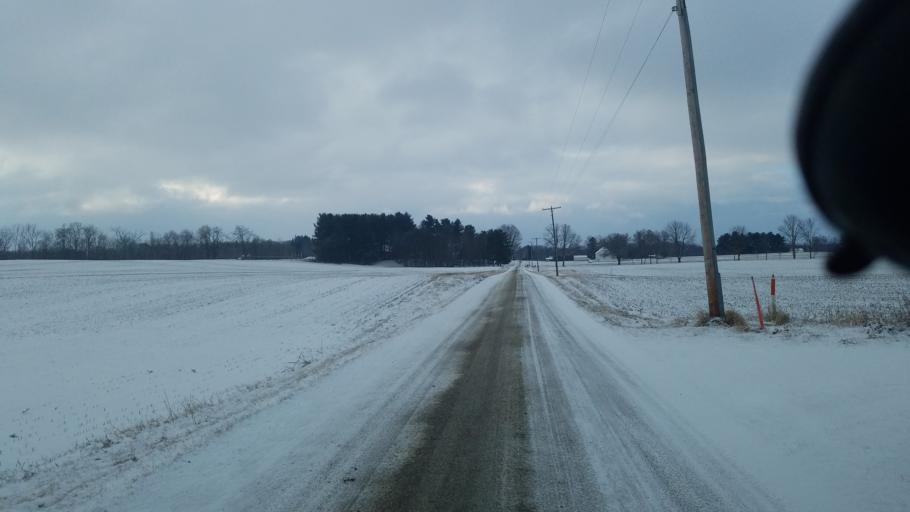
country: US
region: Ohio
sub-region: Morrow County
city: Mount Gilead
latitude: 40.5656
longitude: -82.7962
